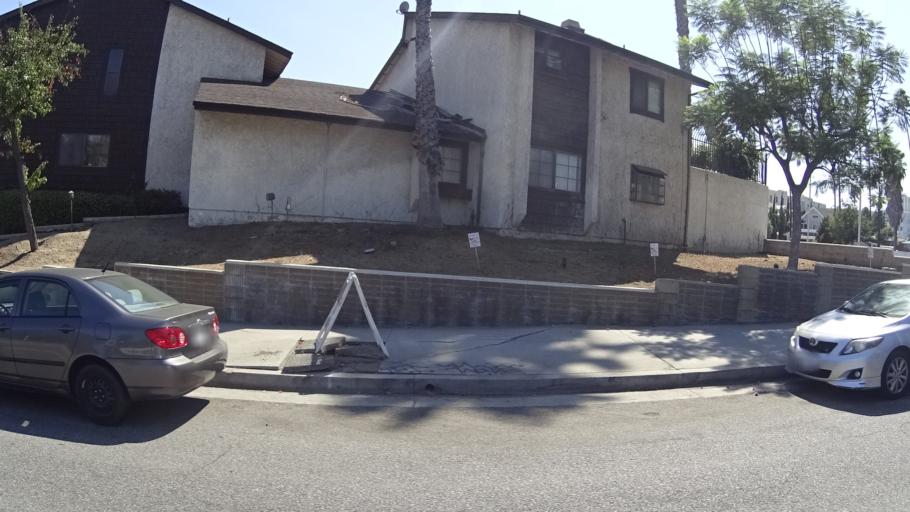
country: US
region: California
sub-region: Los Angeles County
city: Hollywood
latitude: 34.0632
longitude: -118.3158
